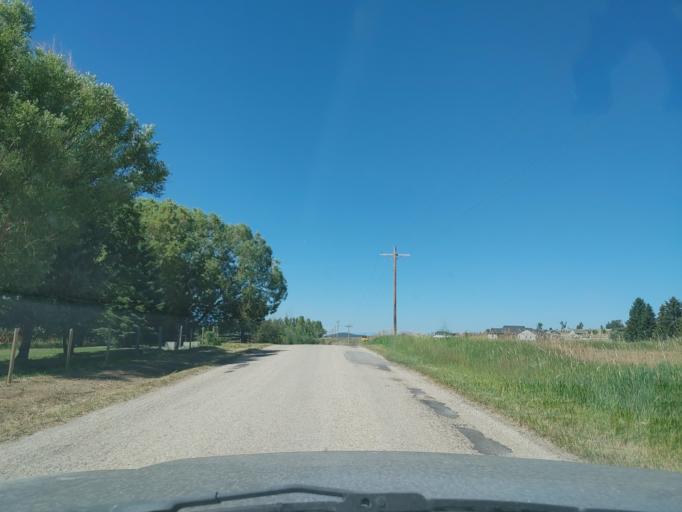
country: US
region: Montana
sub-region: Ravalli County
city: Hamilton
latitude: 46.3429
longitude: -114.0615
